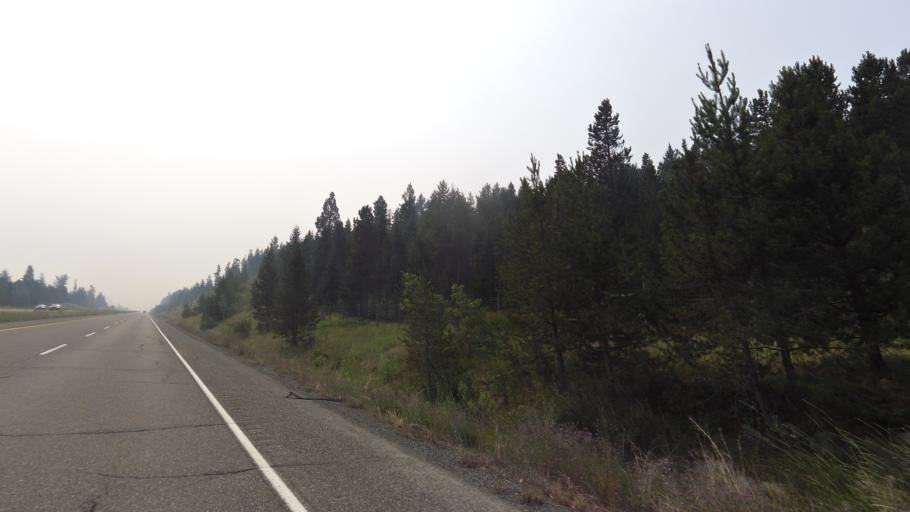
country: CA
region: British Columbia
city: Merritt
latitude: 49.9356
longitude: -120.5403
